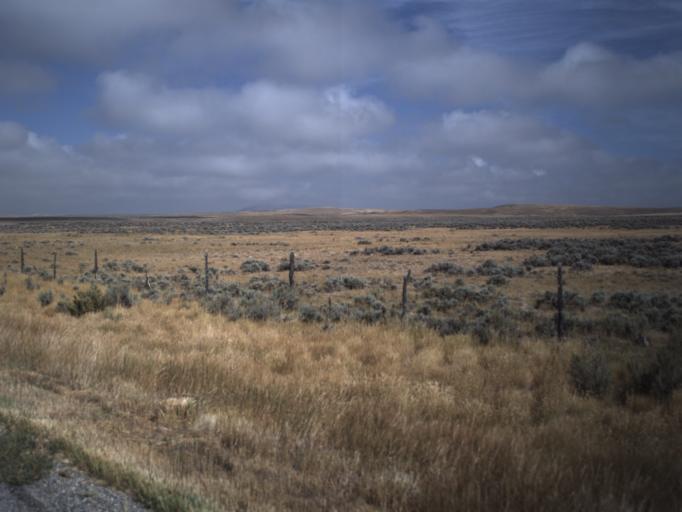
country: US
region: Wyoming
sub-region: Uinta County
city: Evanston
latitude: 41.4513
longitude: -111.0870
